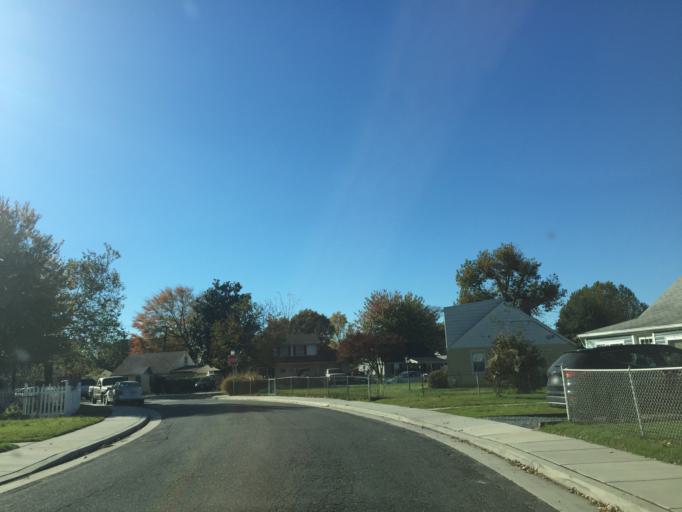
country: US
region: Maryland
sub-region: Baltimore County
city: Dundalk
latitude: 39.2478
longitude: -76.5067
